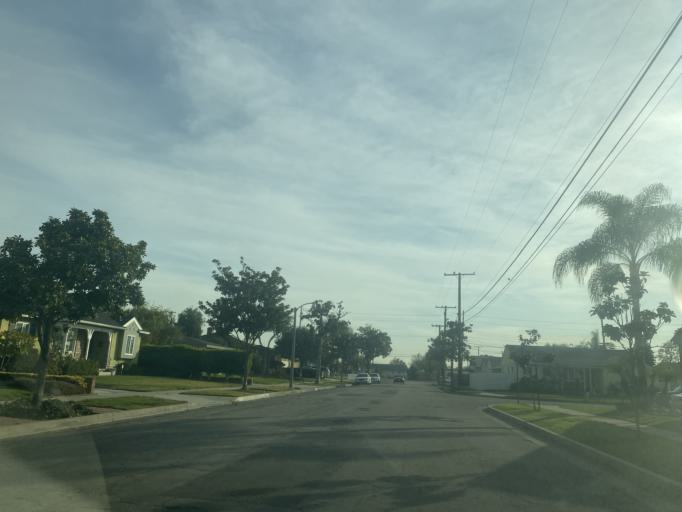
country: US
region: California
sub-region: Orange County
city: Buena Park
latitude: 33.8605
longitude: -117.9637
